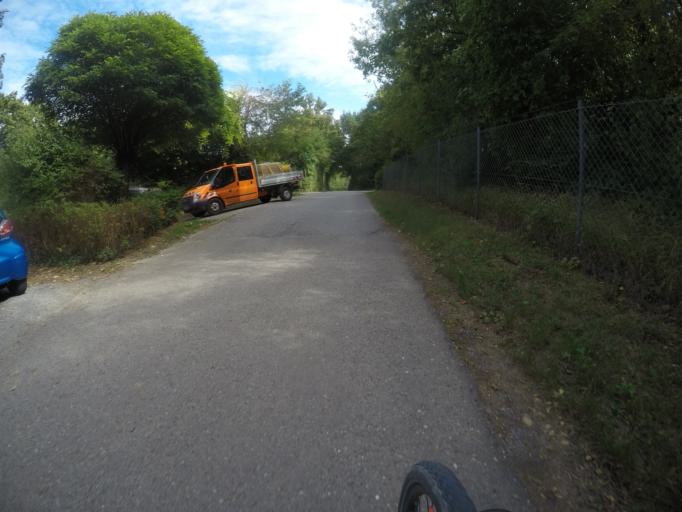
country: DE
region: Baden-Wuerttemberg
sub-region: Regierungsbezirk Stuttgart
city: Tamm
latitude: 48.9061
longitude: 9.1014
